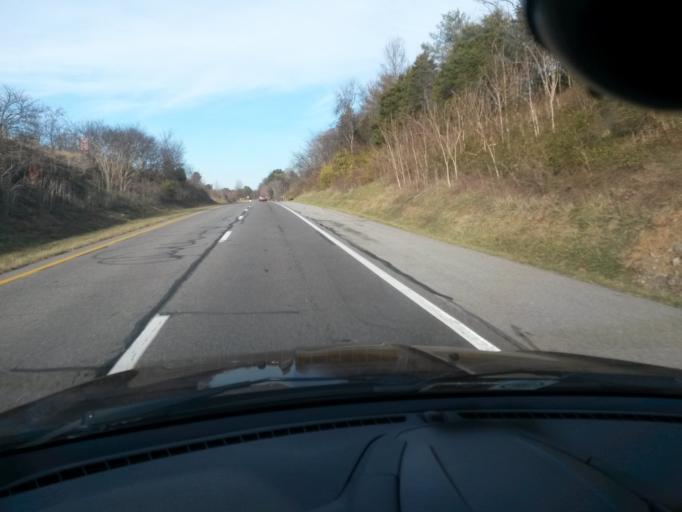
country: US
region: Virginia
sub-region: Botetourt County
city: Fincastle
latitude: 37.4728
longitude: -79.8814
